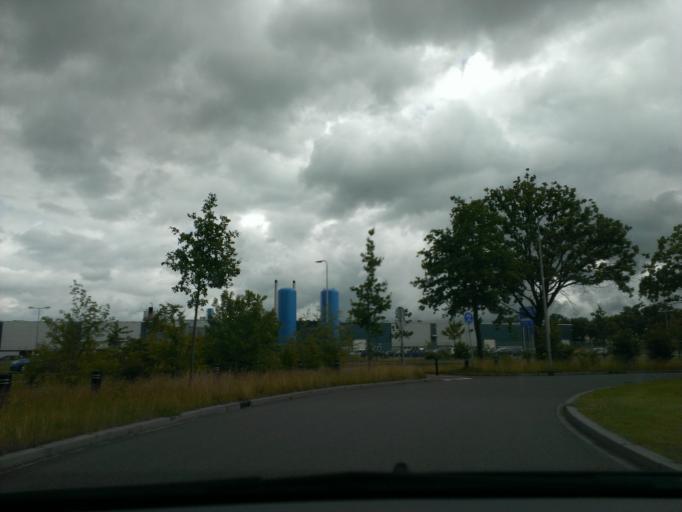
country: NL
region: Drenthe
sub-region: Gemeente Hoogeveen
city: Hoogeveen
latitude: 52.7334
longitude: 6.5037
